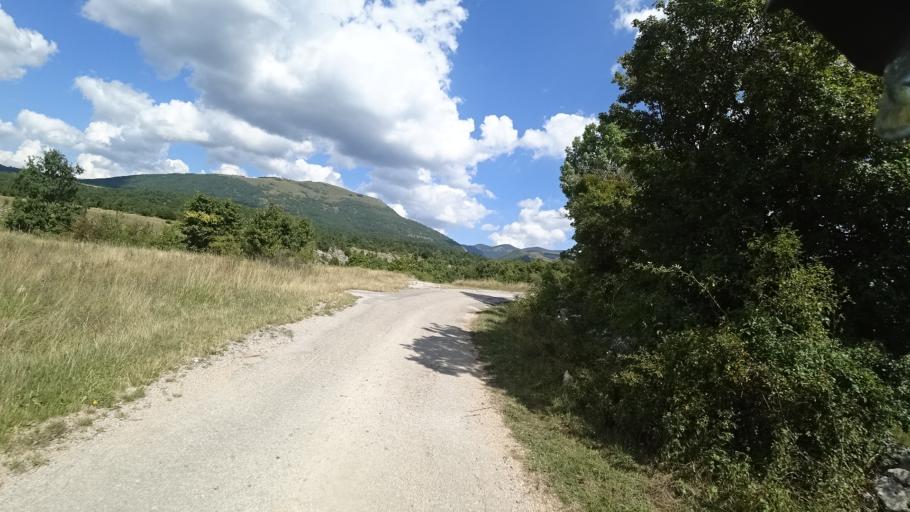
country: HR
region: Zadarska
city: Gracac
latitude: 44.5439
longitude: 15.8060
